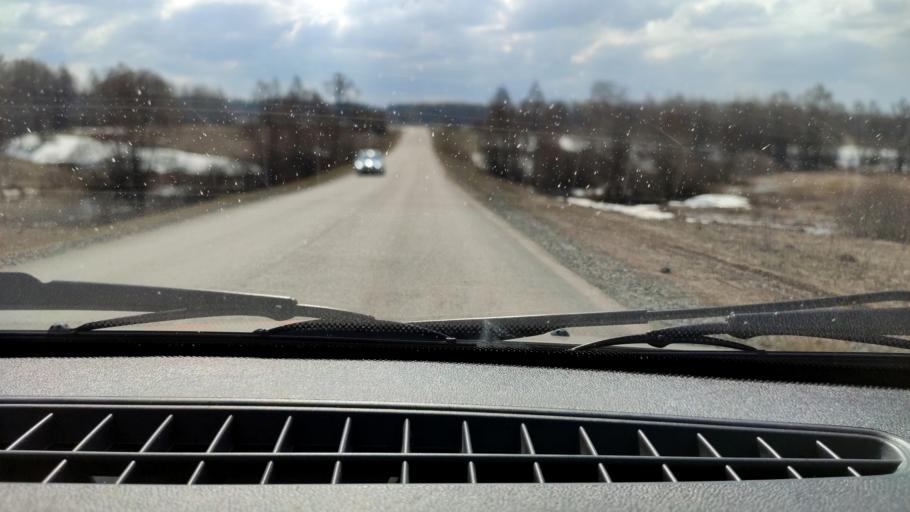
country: RU
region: Bashkortostan
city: Kudeyevskiy
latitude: 54.8200
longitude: 56.7935
